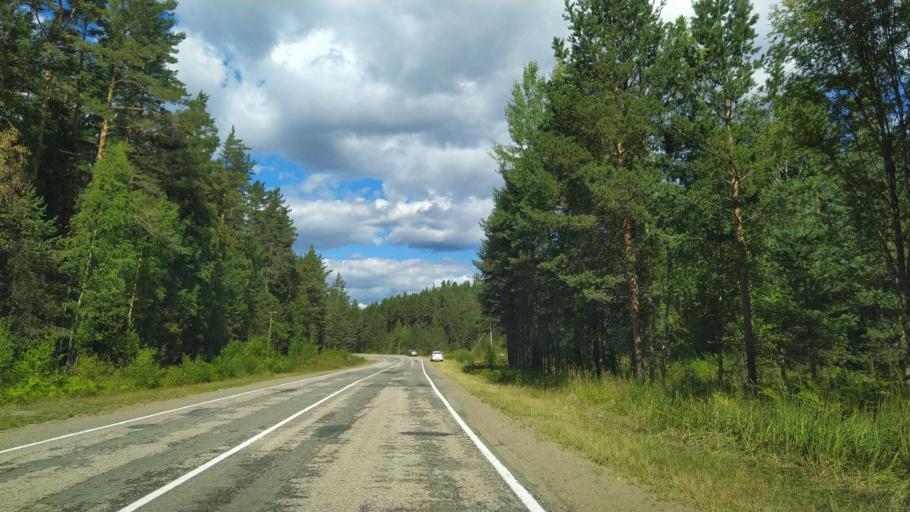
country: RU
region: Leningrad
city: Priozersk
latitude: 60.9940
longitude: 30.2555
